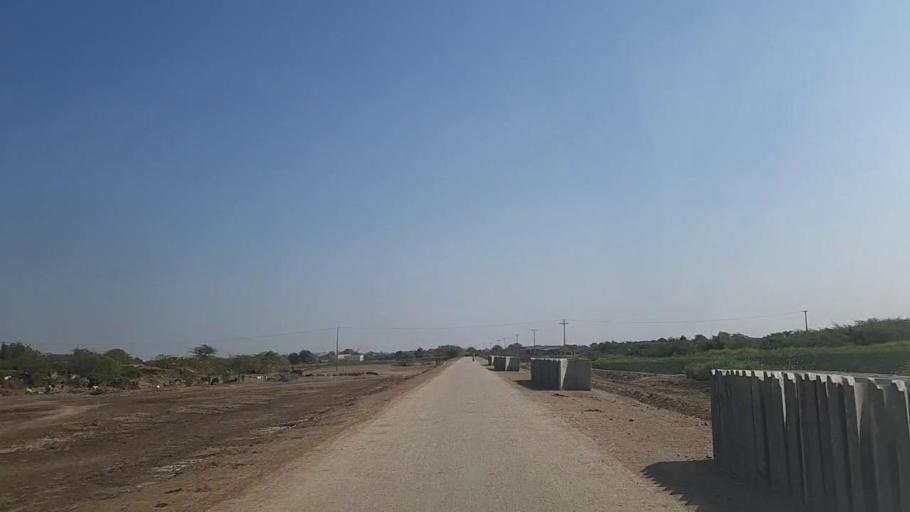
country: PK
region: Sindh
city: Digri
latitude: 25.1600
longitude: 69.1359
